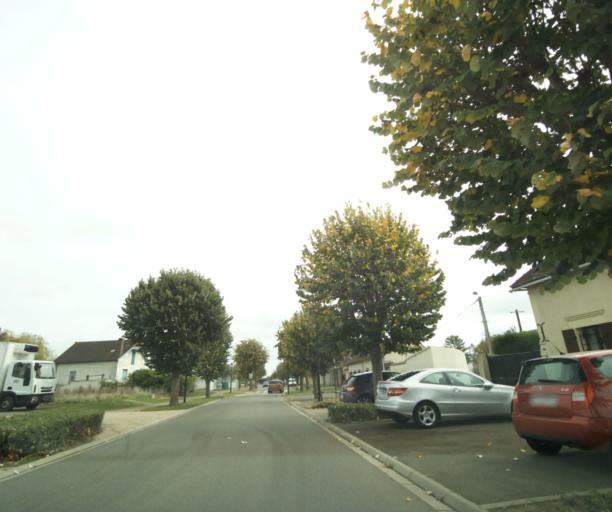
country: FR
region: Centre
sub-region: Departement d'Eure-et-Loir
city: Dreux
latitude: 48.7412
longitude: 1.3418
